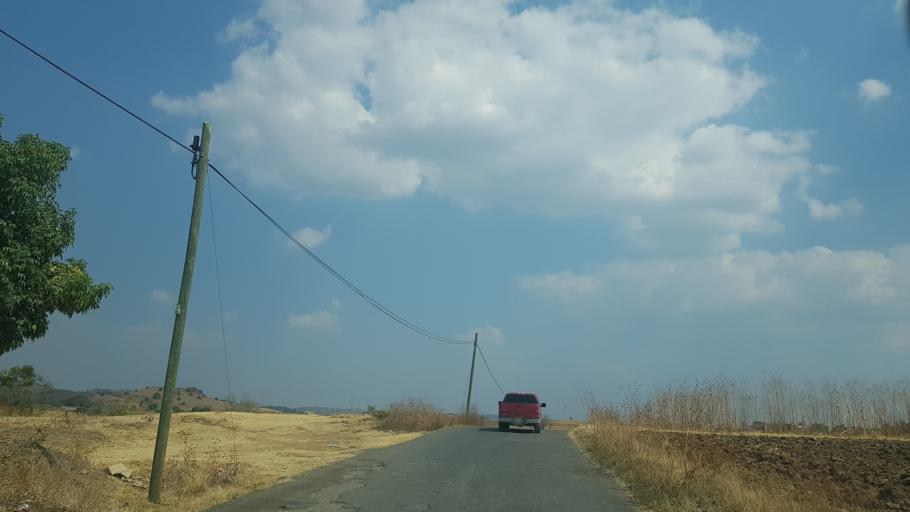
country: MX
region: Puebla
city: San Juan Amecac
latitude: 18.8216
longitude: -98.6541
